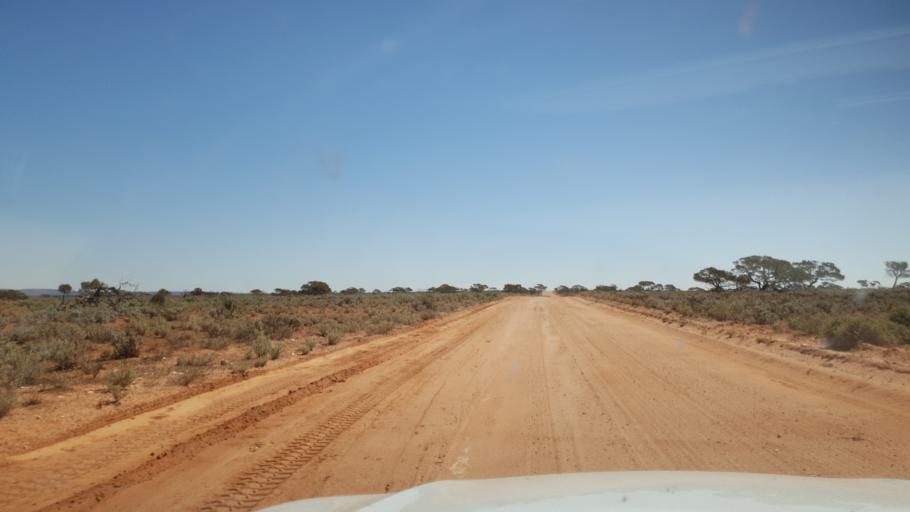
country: AU
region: South Australia
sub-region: Whyalla
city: Whyalla
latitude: -32.6395
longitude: 136.9245
